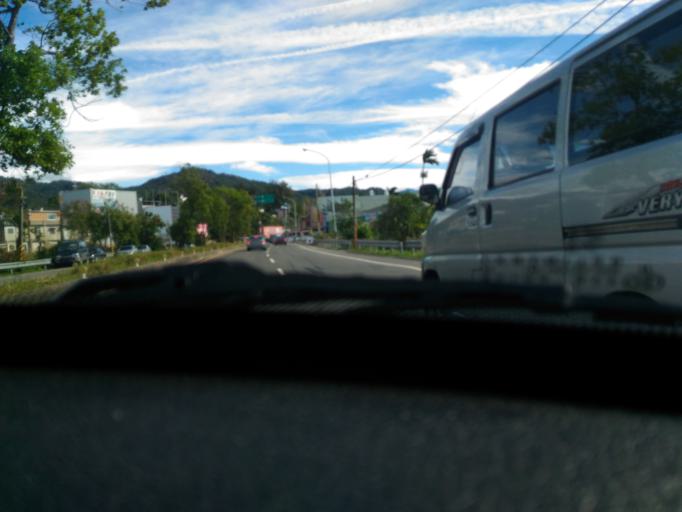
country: TW
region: Taiwan
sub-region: Hsinchu
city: Zhubei
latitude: 24.7635
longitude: 121.0875
